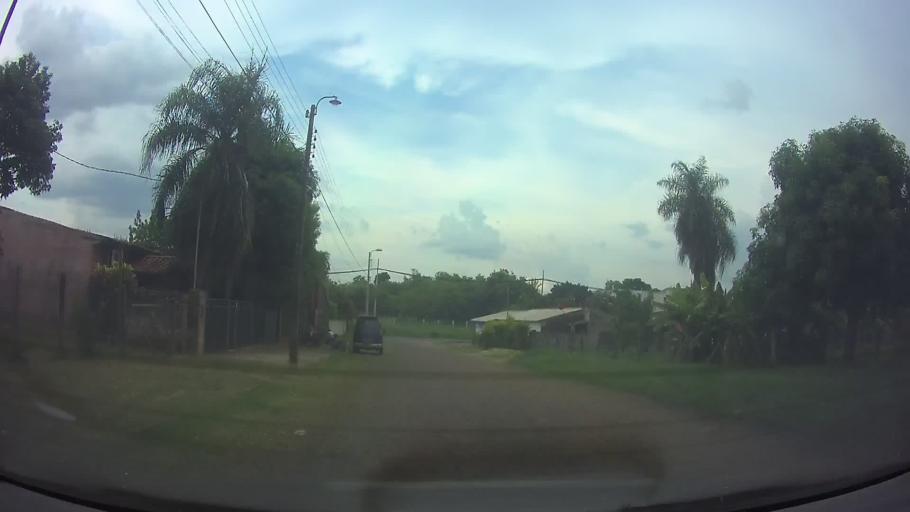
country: PY
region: Central
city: San Lorenzo
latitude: -25.2803
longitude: -57.4932
